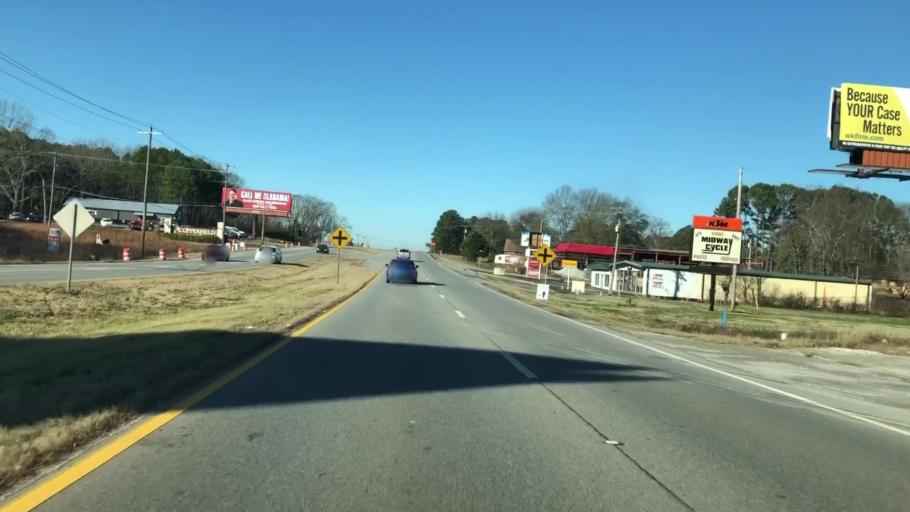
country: US
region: Alabama
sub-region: Madison County
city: Madison
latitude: 34.7481
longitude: -86.7885
